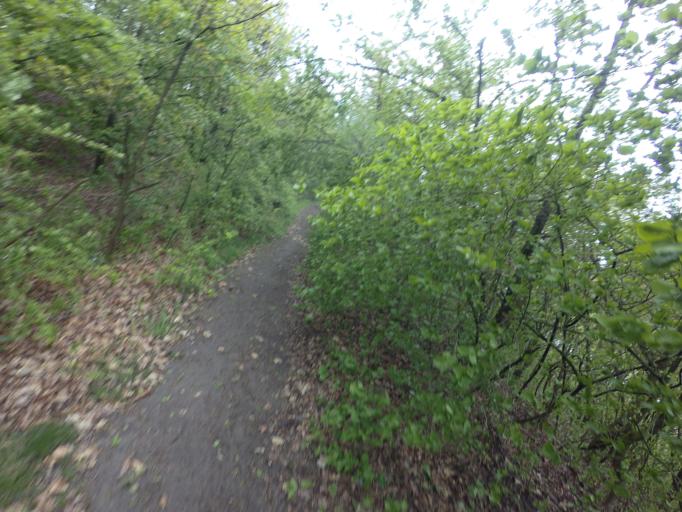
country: NL
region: Limburg
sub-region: Gemeente Kerkrade
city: Kerkrade
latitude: 50.8840
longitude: 6.0269
